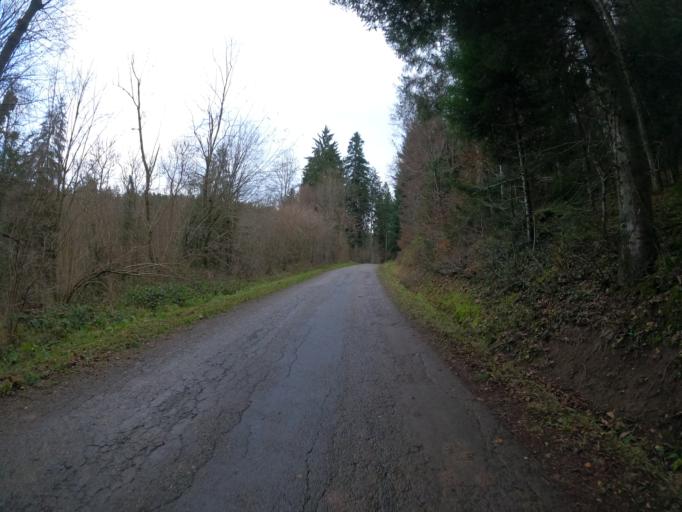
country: DE
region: Baden-Wuerttemberg
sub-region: Regierungsbezirk Stuttgart
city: Waschenbeuren
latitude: 48.7698
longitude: 9.7134
